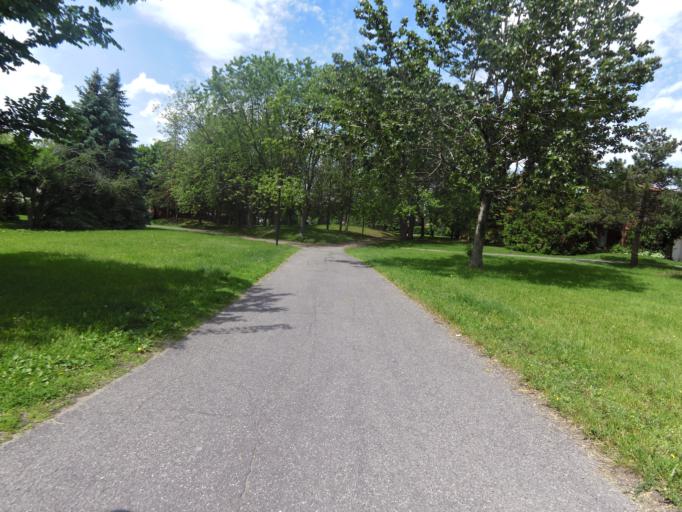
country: CA
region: Ontario
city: Ottawa
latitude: 45.3607
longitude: -75.6439
